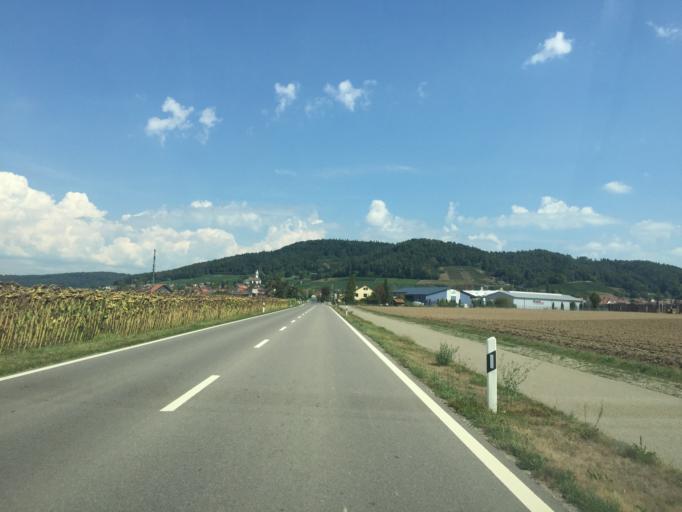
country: CH
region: Thurgau
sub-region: Frauenfeld District
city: Diessenhofen
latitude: 47.6284
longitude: 8.7840
